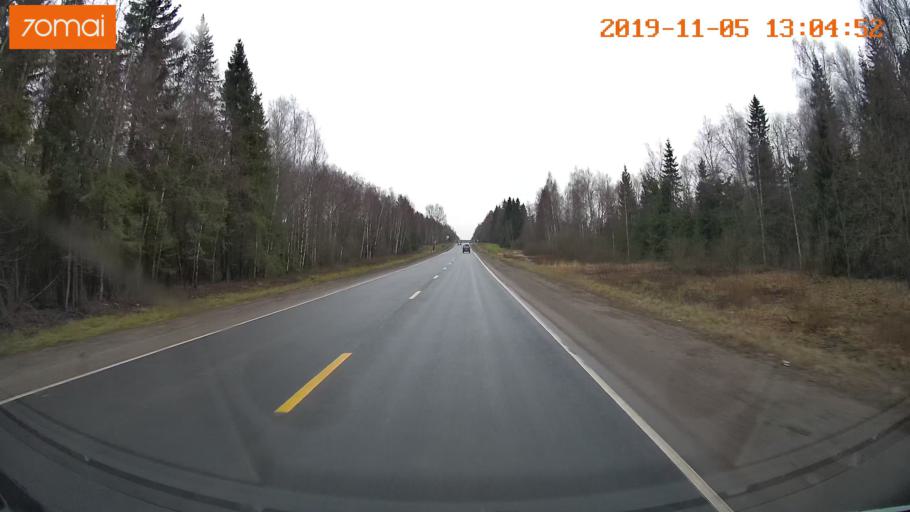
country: RU
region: Ivanovo
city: Kitovo
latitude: 56.8863
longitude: 41.2305
